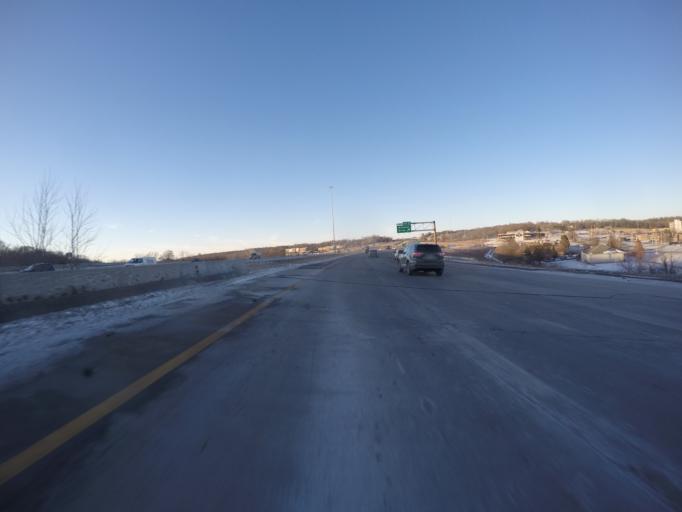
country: US
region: Kansas
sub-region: Johnson County
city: Lenexa
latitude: 38.9962
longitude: -94.7810
